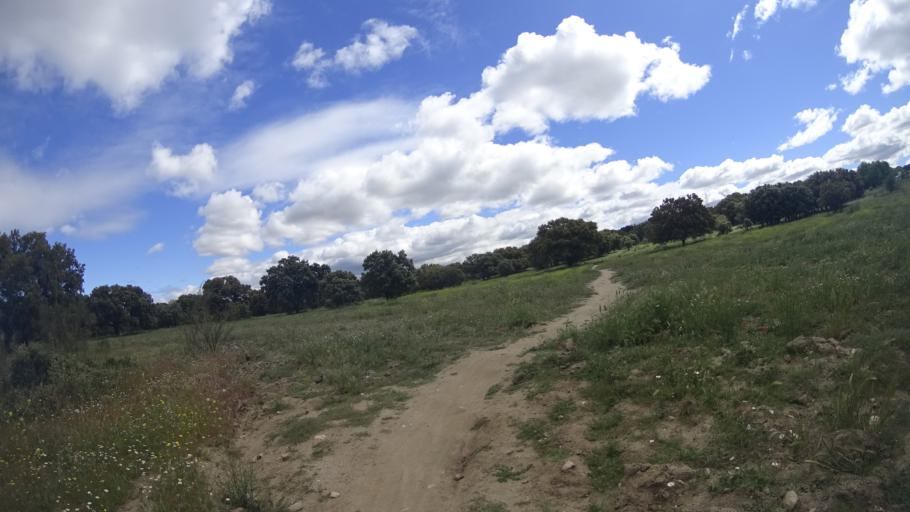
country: ES
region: Madrid
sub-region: Provincia de Madrid
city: Brunete
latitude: 40.4150
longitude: -3.9478
